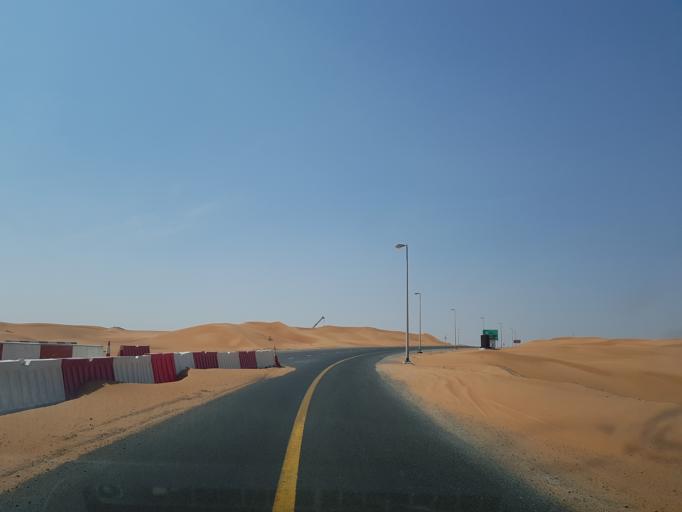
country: AE
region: Ash Shariqah
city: Adh Dhayd
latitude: 25.2490
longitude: 55.8213
